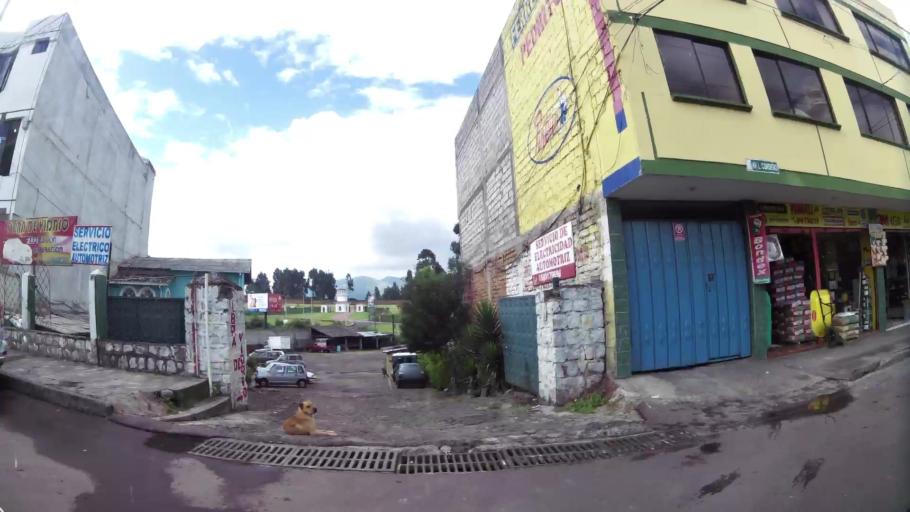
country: EC
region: Pichincha
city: Sangolqui
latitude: -0.3253
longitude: -78.4475
